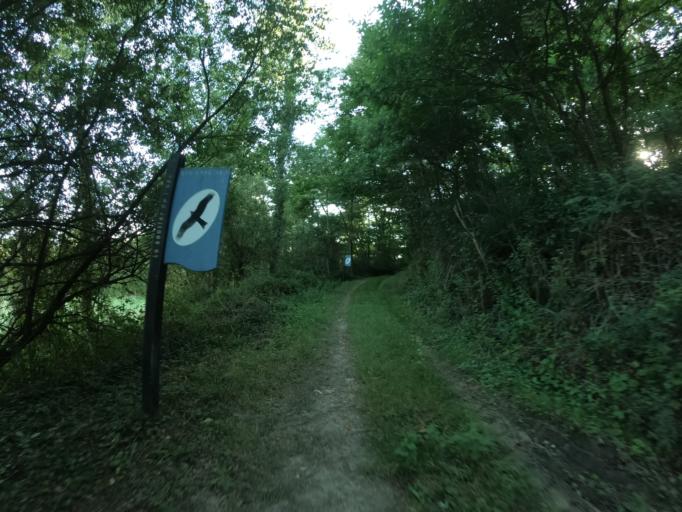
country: FR
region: Midi-Pyrenees
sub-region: Departement de l'Ariege
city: La Tour-du-Crieu
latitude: 43.0993
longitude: 1.7139
